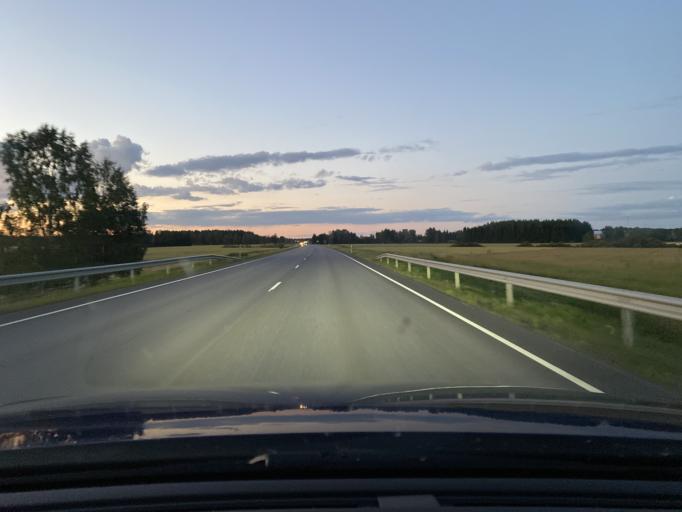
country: FI
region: Varsinais-Suomi
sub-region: Loimaa
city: Oripaeae
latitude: 60.8437
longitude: 22.6763
